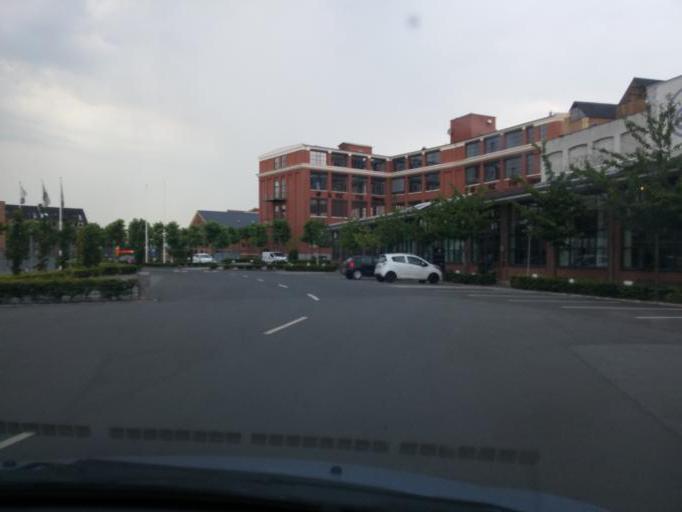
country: DK
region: South Denmark
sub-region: Odense Kommune
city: Odense
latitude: 55.4056
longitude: 10.3903
